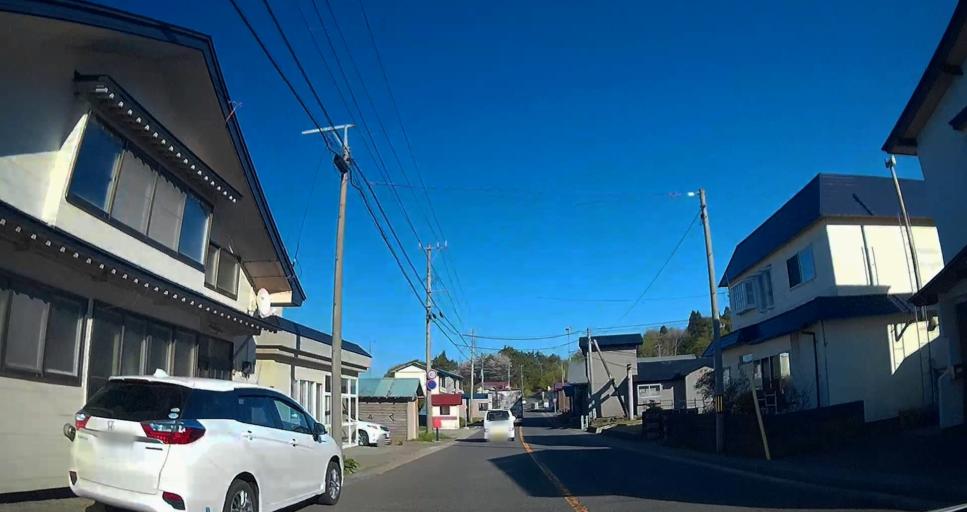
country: JP
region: Aomori
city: Mutsu
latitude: 41.4552
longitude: 141.1159
